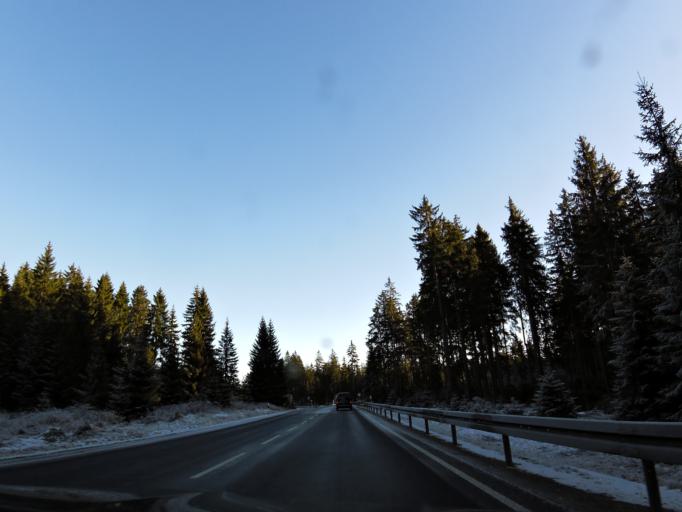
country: DE
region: Bavaria
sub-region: Upper Franconia
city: Fichtelberg
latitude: 50.0298
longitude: 11.8523
